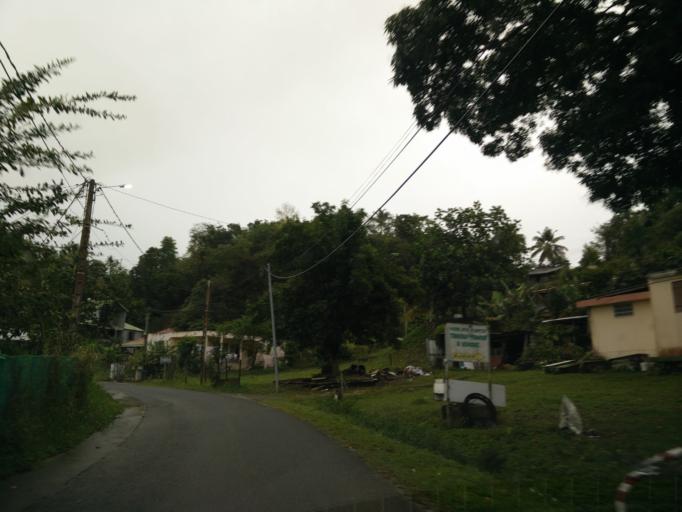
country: GP
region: Guadeloupe
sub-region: Guadeloupe
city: Le Gosier
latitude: 16.2362
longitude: -61.4898
